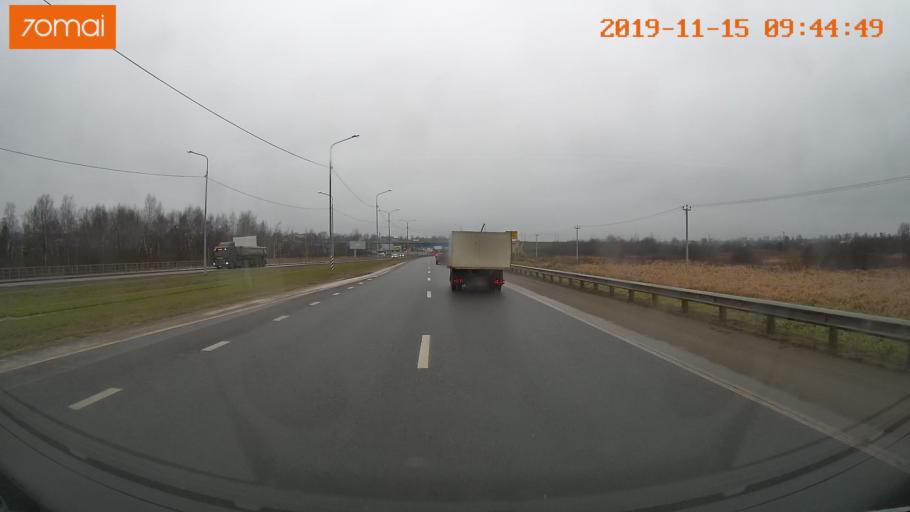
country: RU
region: Vologda
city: Sheksna
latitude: 59.2116
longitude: 38.5248
